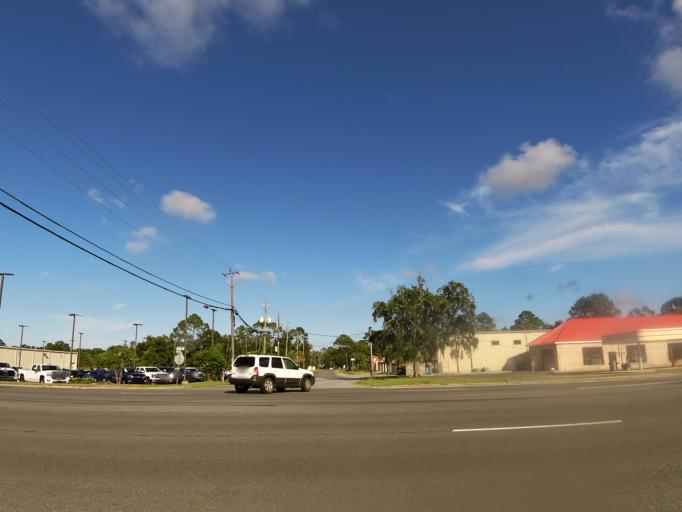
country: US
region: Georgia
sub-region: Glynn County
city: Country Club Estates
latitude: 31.2066
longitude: -81.4827
